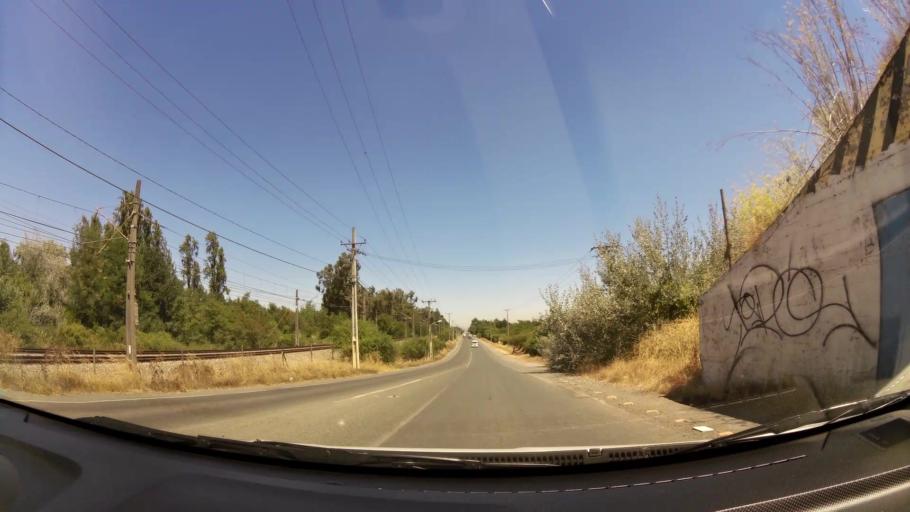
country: CL
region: O'Higgins
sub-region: Provincia de Cachapoal
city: Rancagua
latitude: -34.2319
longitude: -70.7872
